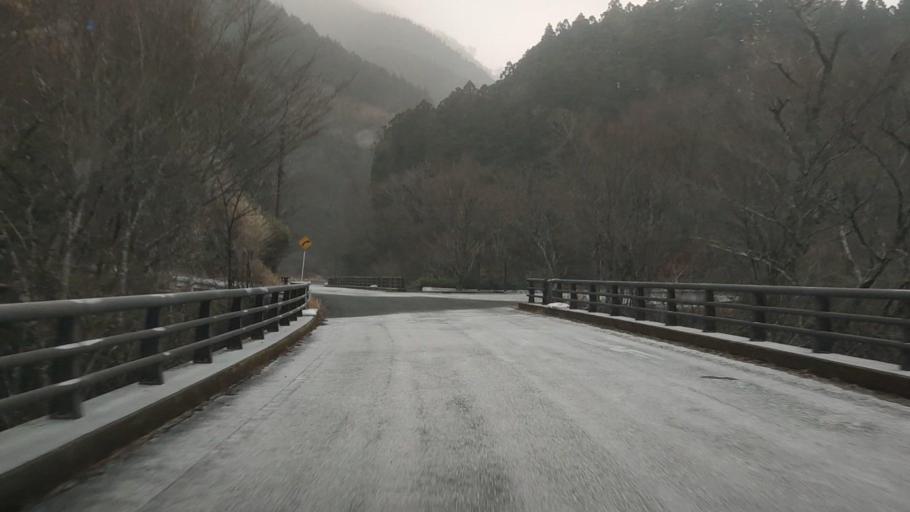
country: JP
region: Kumamoto
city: Matsubase
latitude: 32.5655
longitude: 130.9119
